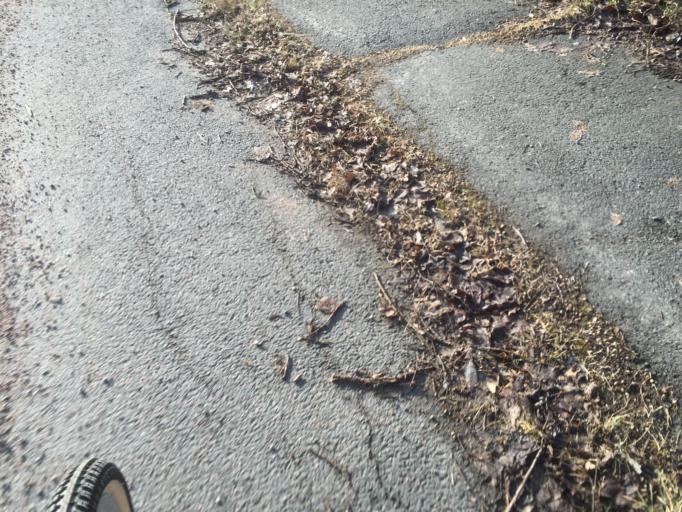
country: SE
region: Joenkoeping
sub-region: Aneby Kommun
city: Aneby
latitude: 57.8371
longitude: 14.8033
